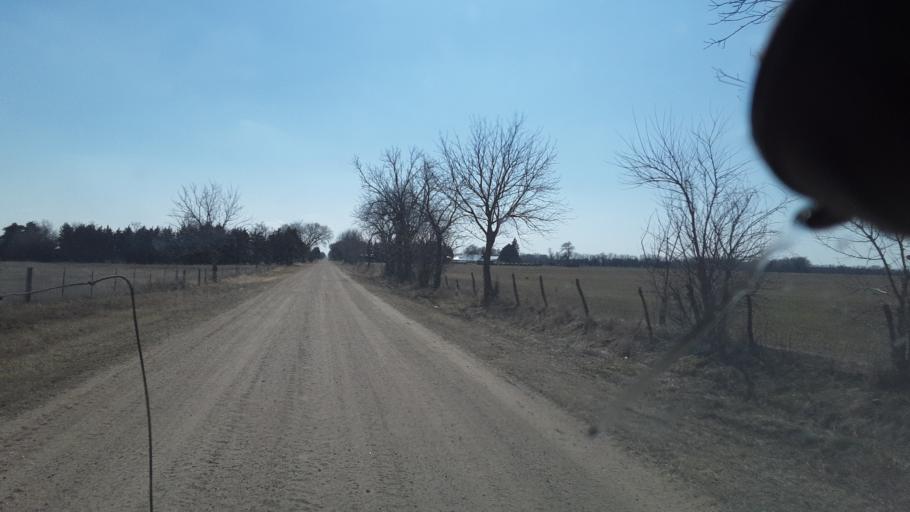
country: US
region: Kansas
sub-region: Reno County
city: Haven
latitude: 37.9194
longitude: -97.8484
